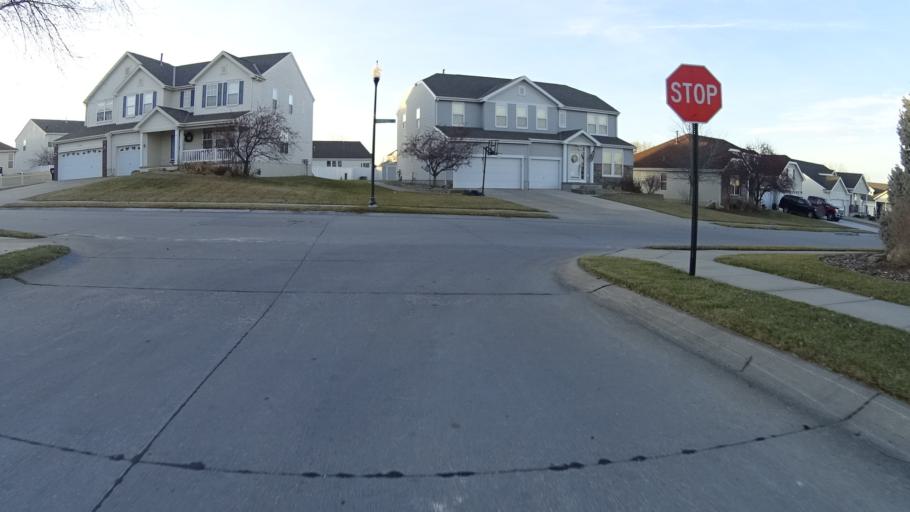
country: US
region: Nebraska
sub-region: Sarpy County
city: Papillion
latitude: 41.1313
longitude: -96.0690
